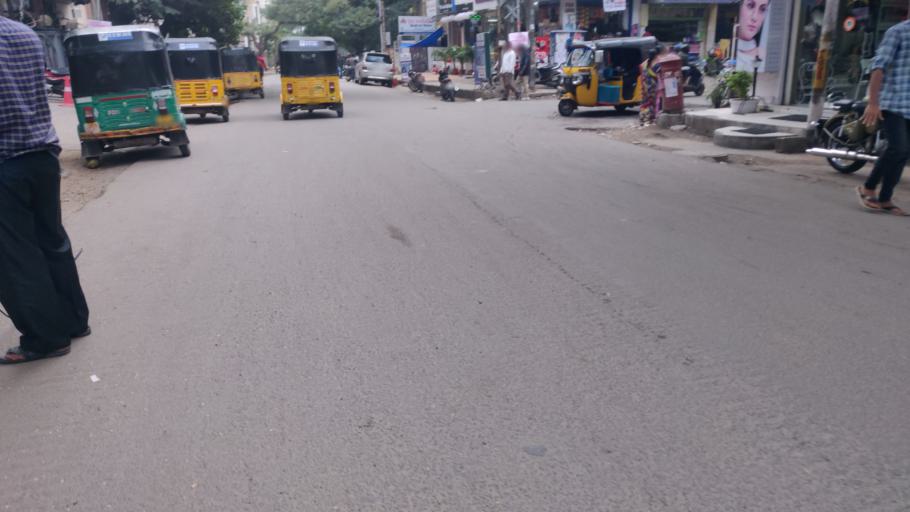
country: IN
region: Telangana
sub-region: Hyderabad
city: Hyderabad
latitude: 17.3921
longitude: 78.4376
